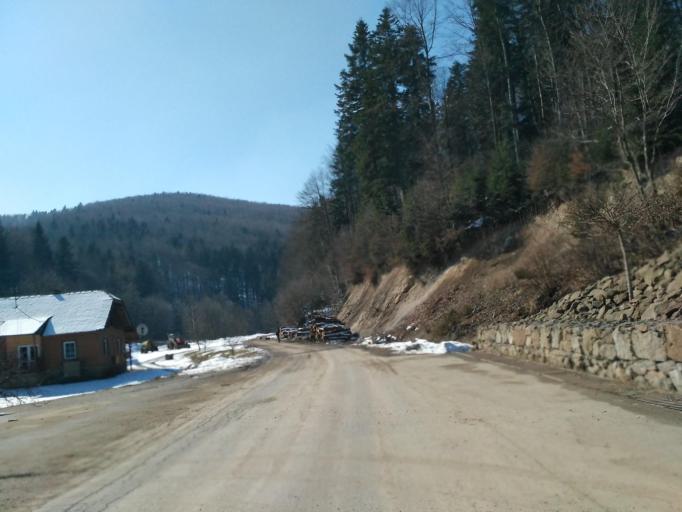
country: PL
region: Subcarpathian Voivodeship
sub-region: Powiat brzozowski
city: Jablonica Polska
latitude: 49.7517
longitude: 21.8664
